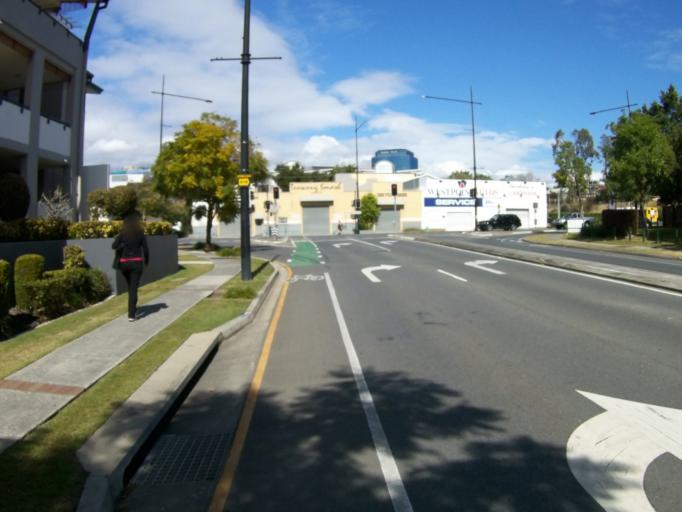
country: AU
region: Queensland
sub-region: Brisbane
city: Toowong
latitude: -27.4815
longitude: 152.9955
